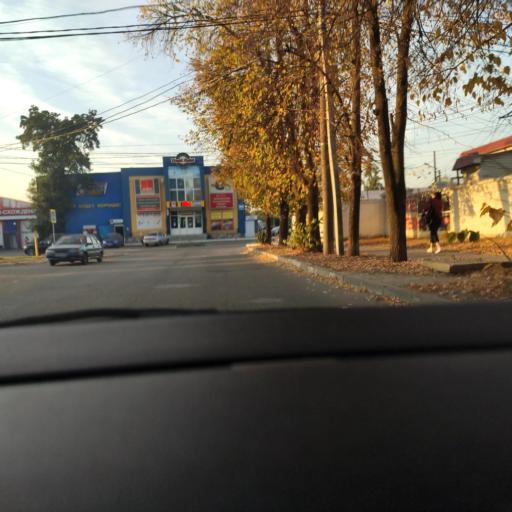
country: RU
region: Voronezj
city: Voronezh
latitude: 51.6618
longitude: 39.1335
